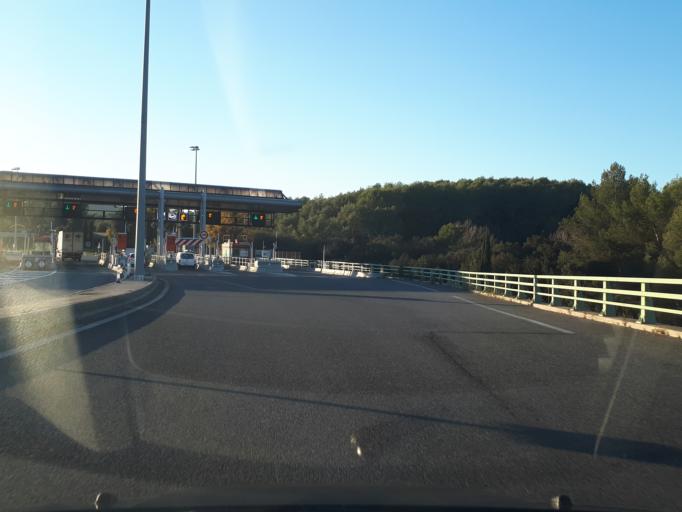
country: FR
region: Provence-Alpes-Cote d'Azur
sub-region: Departement des Alpes-Maritimes
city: Vallauris
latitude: 43.6050
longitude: 7.0675
